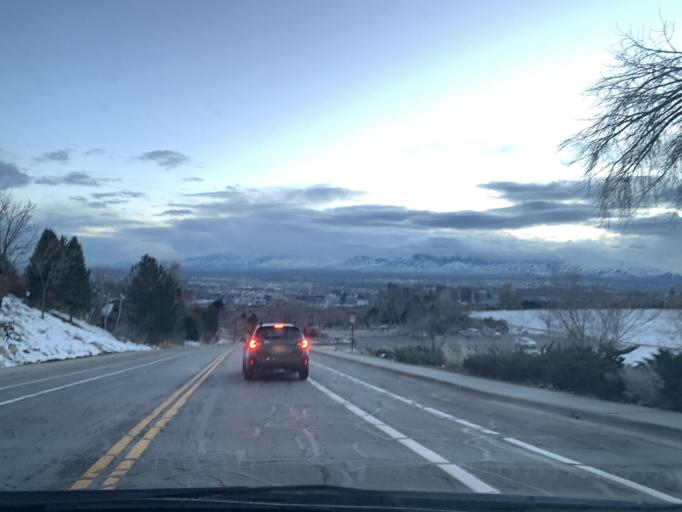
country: US
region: Utah
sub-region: Salt Lake County
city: Salt Lake City
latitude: 40.7828
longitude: -111.8611
